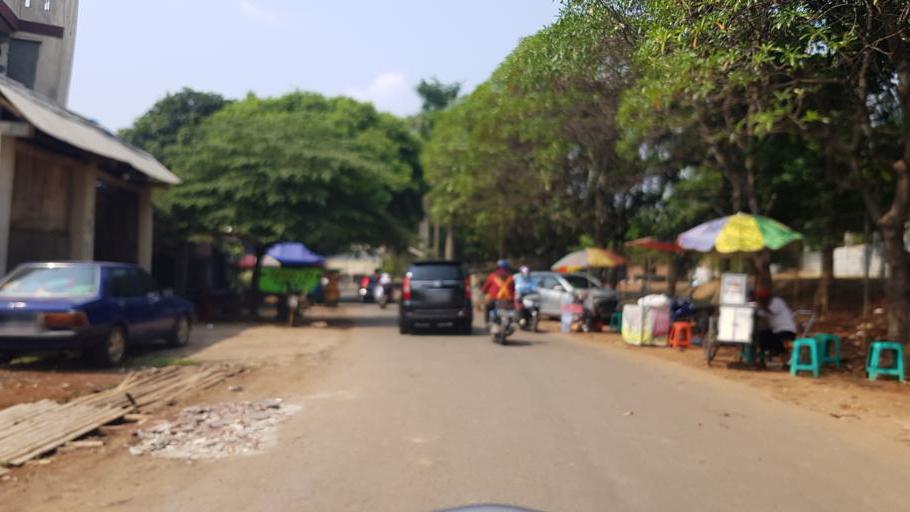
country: ID
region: West Java
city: Bekasi
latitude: -6.2846
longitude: 106.9298
